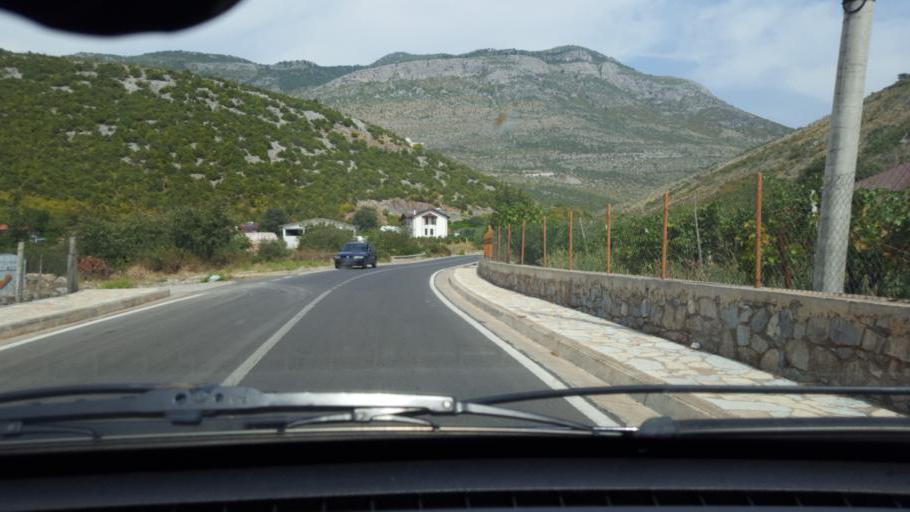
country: AL
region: Shkoder
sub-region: Rrethi i Malesia e Madhe
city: Hot
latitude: 42.3646
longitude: 19.4455
